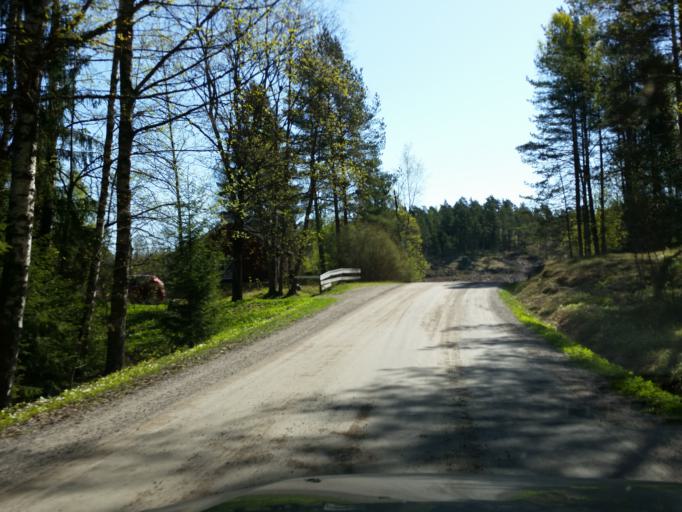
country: FI
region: Uusimaa
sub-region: Helsinki
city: Karjalohja
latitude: 60.1828
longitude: 23.6794
